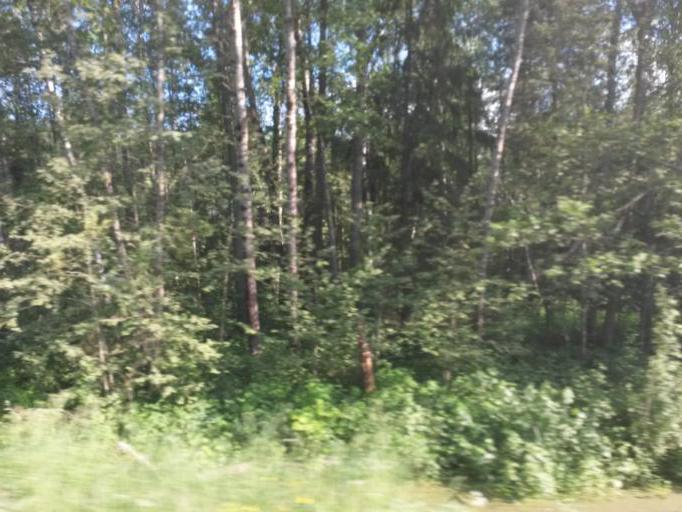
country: RU
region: Jaroslavl
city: Dubki
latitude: 57.2993
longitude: 40.0669
